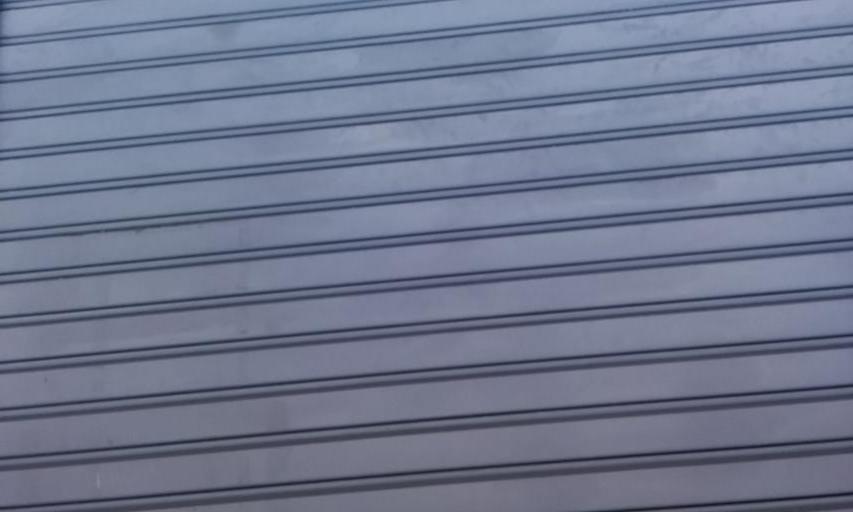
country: JP
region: Tokyo
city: Urayasu
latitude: 35.7008
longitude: 139.8494
